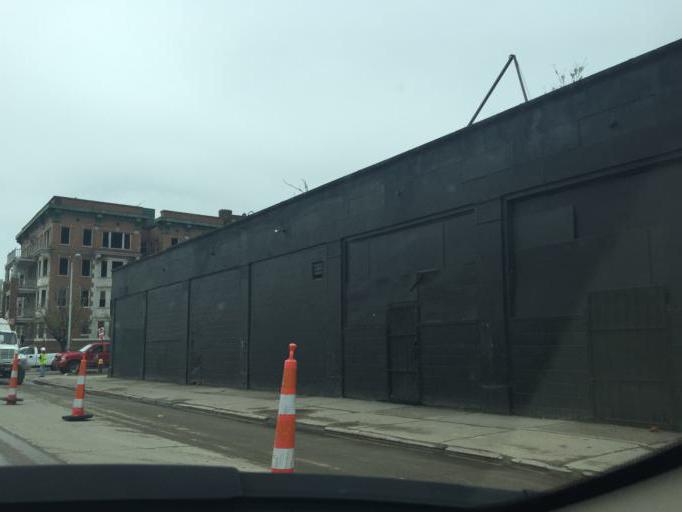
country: US
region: Michigan
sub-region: Wayne County
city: Detroit
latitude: 42.3395
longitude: -83.0573
